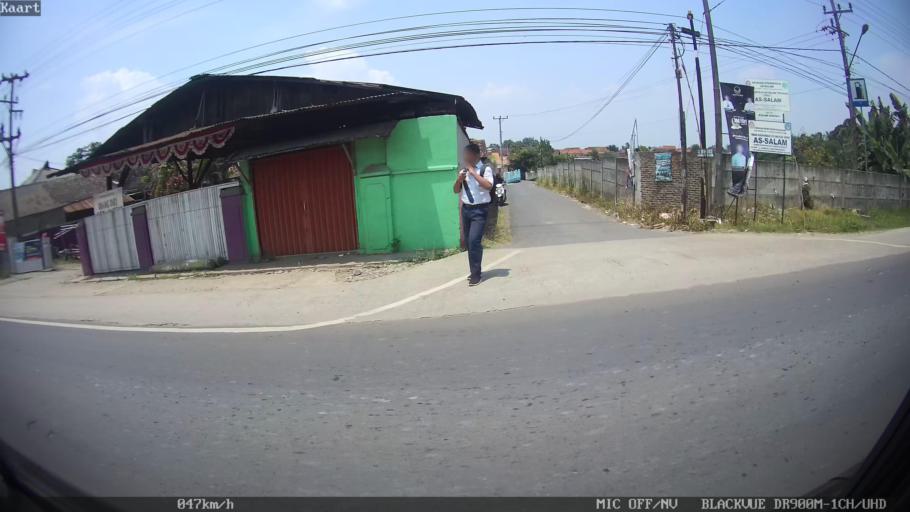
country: ID
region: Lampung
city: Natar
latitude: -5.3381
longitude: 105.2121
